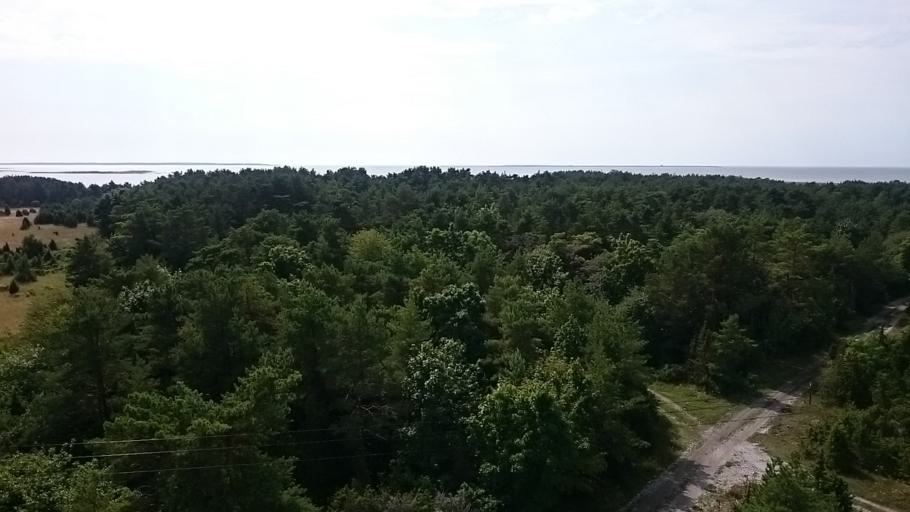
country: EE
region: Saare
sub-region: Kuressaare linn
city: Kuressaare
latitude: 58.3781
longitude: 21.8426
